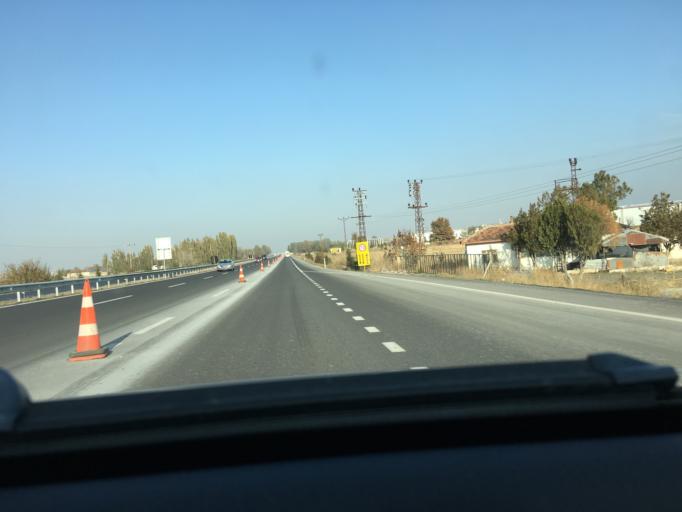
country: TR
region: Ankara
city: Temelli
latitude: 39.6843
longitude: 32.2450
